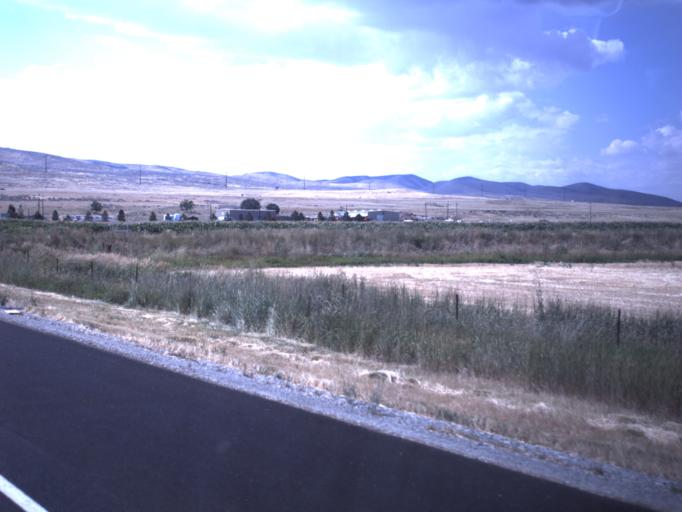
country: US
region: Utah
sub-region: Box Elder County
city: Garland
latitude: 41.7848
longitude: -112.1597
